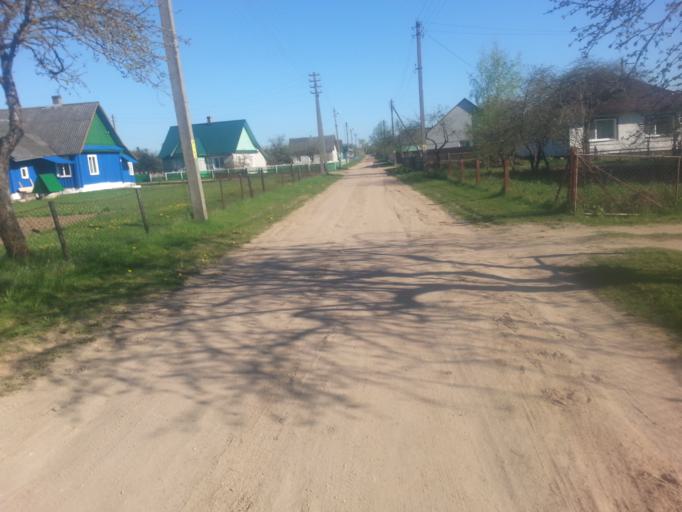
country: BY
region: Minsk
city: Narach
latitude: 54.9340
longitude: 26.6791
